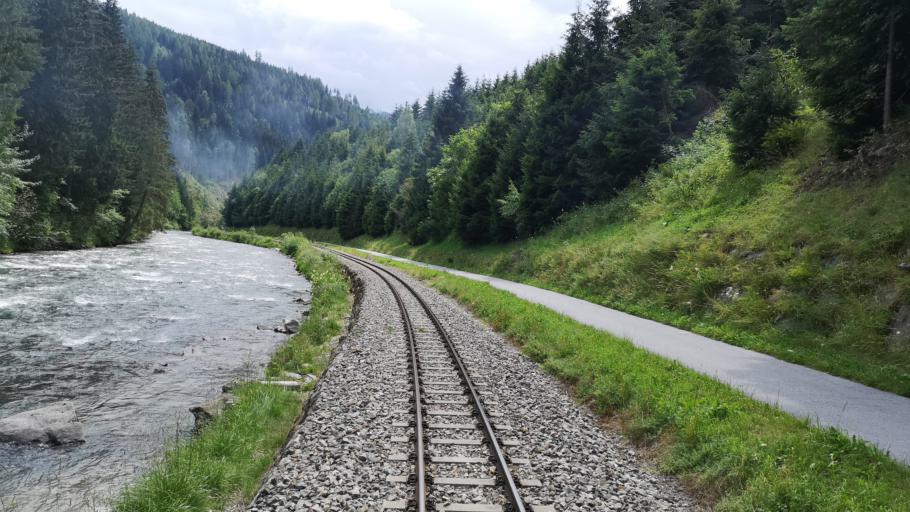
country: AT
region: Salzburg
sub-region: Politischer Bezirk Tamsweg
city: Ramingstein
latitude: 47.0936
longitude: 13.8201
